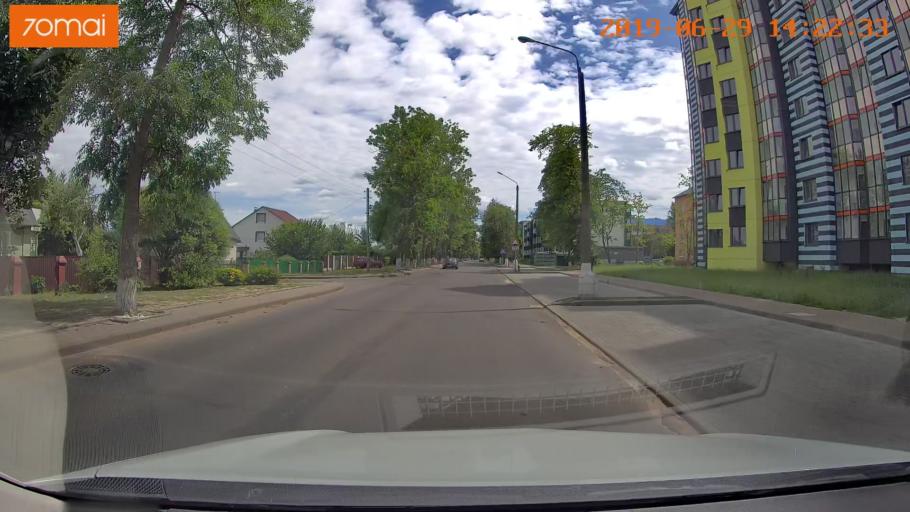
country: BY
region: Minsk
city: Salihorsk
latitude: 52.7911
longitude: 27.5506
